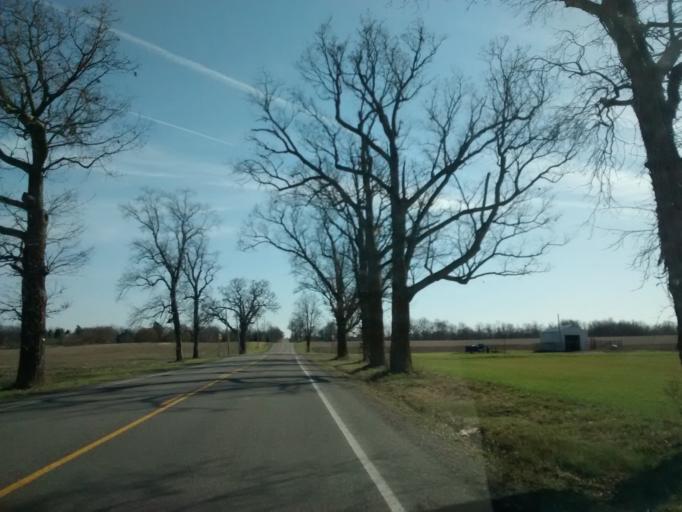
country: US
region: New York
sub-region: Livingston County
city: Avon
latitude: 42.9356
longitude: -77.7783
